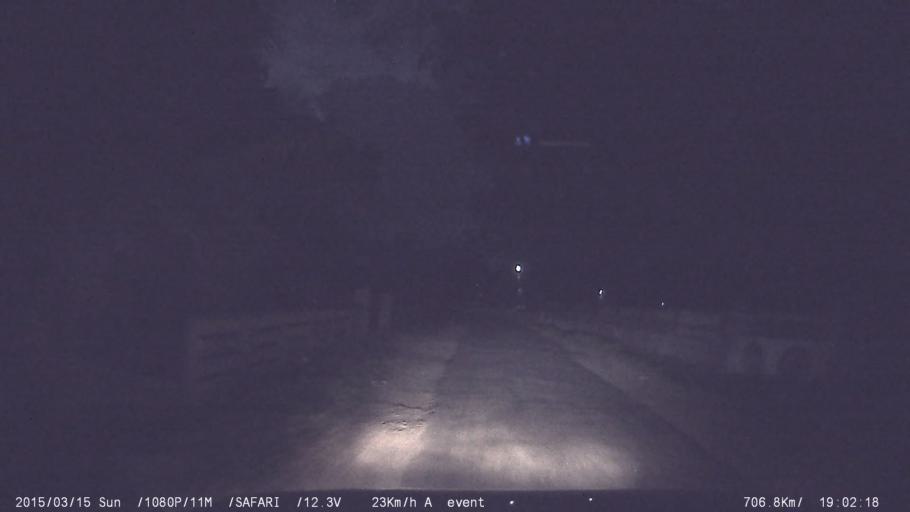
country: IN
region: Kerala
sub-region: Ernakulam
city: Muvattupuzha
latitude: 9.8765
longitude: 76.6496
